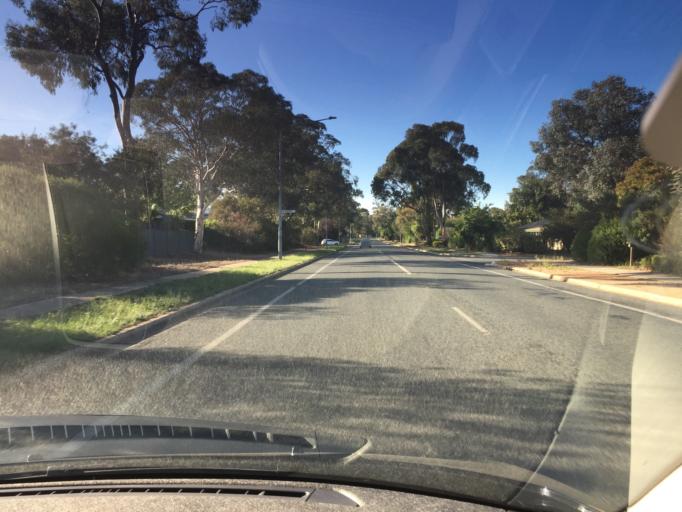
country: AU
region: Australian Capital Territory
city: Kaleen
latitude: -35.2254
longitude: 149.1111
